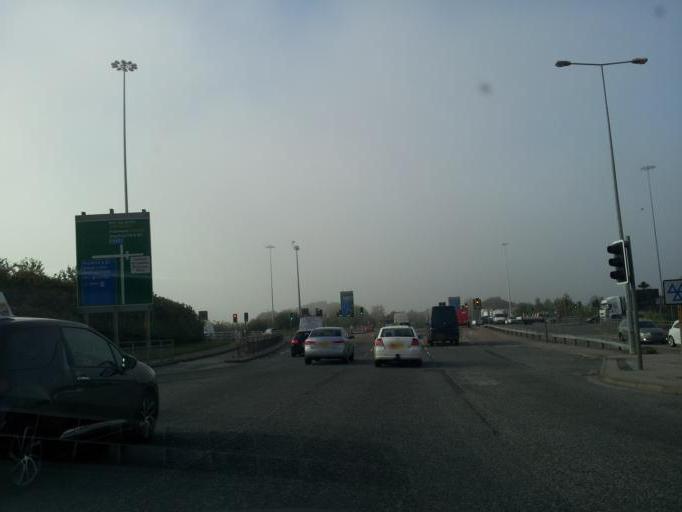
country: GB
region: England
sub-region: Manchester
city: Failsworth
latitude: 53.5279
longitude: -2.1586
